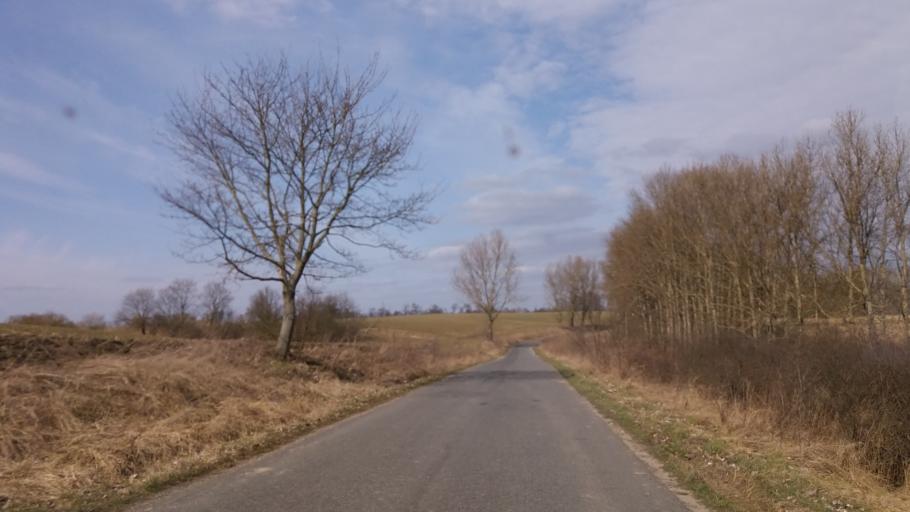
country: PL
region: West Pomeranian Voivodeship
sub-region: Powiat choszczenski
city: Krzecin
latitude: 53.1314
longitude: 15.5465
